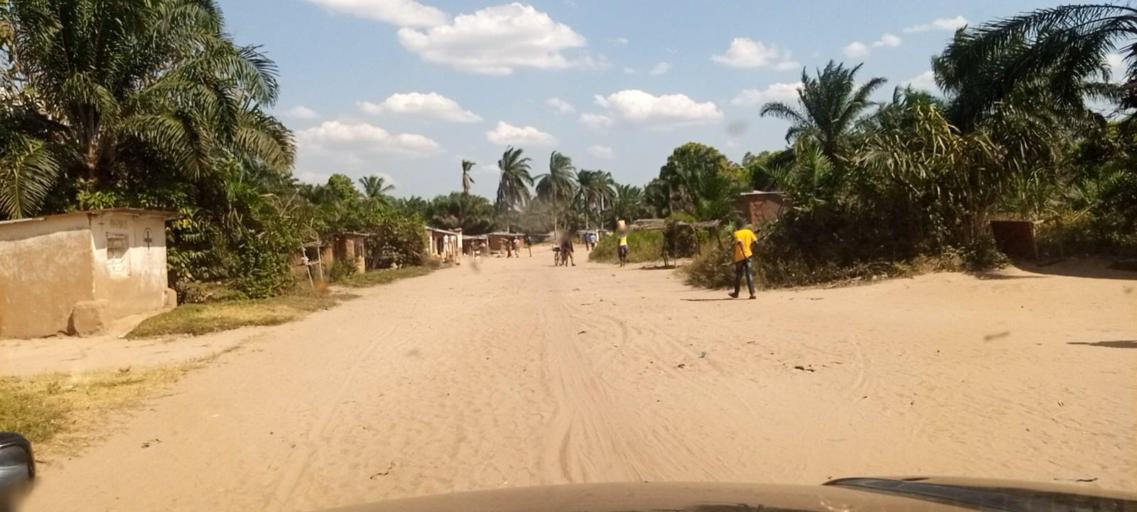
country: CD
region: Kasai-Oriental
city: Kabinda
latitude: -6.1292
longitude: 24.5264
